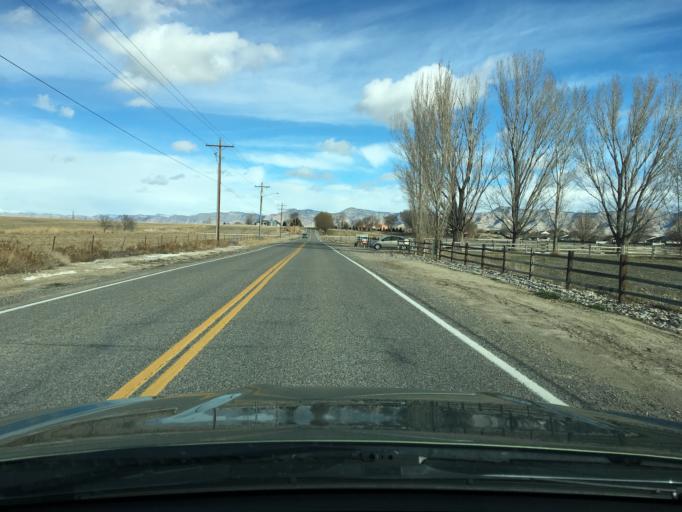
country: US
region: Colorado
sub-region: Mesa County
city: Grand Junction
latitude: 39.1269
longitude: -108.5616
